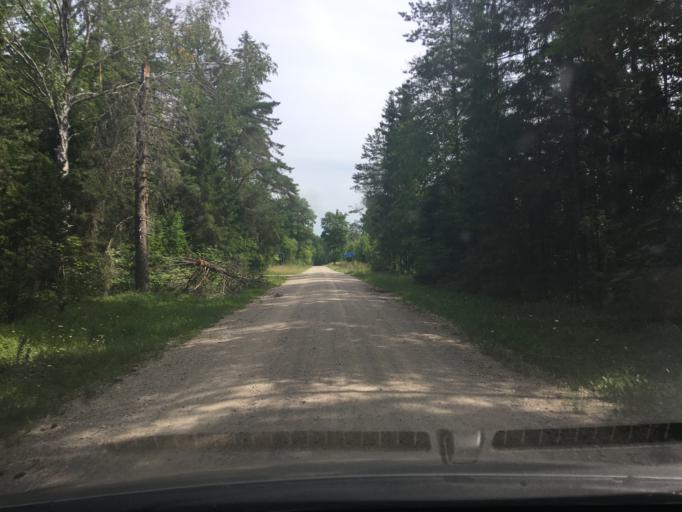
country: EE
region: Raplamaa
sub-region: Maerjamaa vald
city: Marjamaa
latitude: 58.9509
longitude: 24.5724
